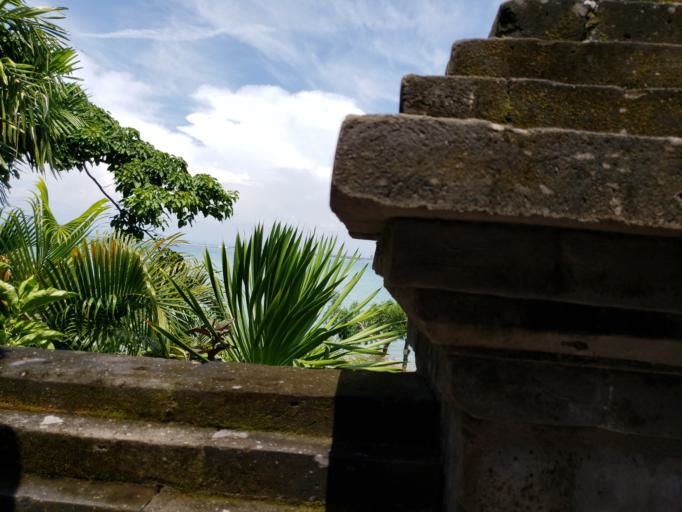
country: ID
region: Bali
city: Jimbaran
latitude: -8.7816
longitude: 115.1570
